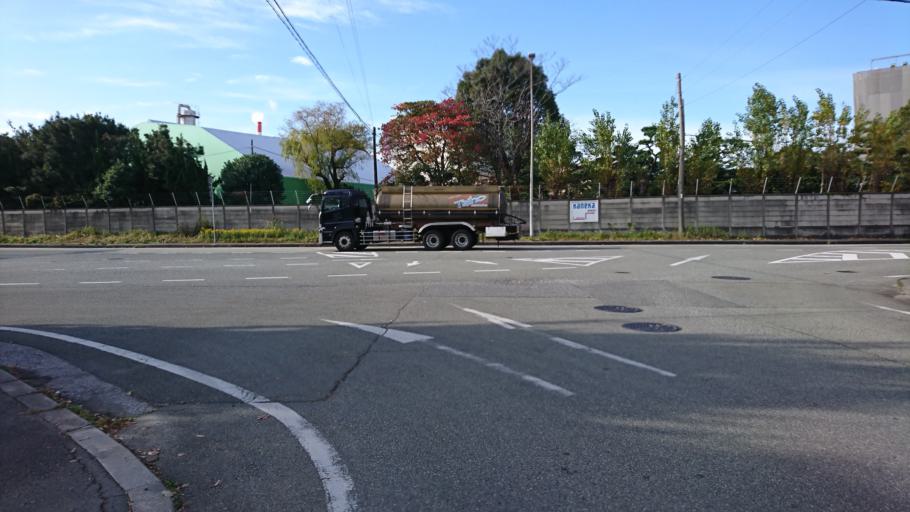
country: JP
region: Hyogo
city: Kakogawacho-honmachi
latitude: 34.7431
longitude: 134.8009
